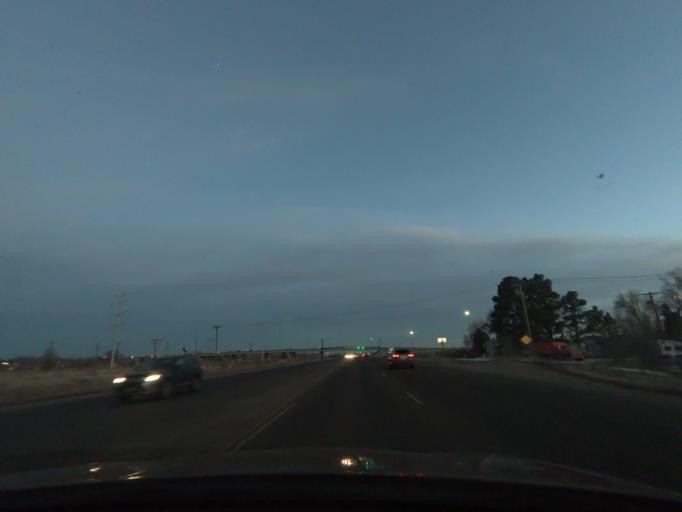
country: US
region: Colorado
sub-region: El Paso County
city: Stratmoor
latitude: 38.7706
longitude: -104.7637
